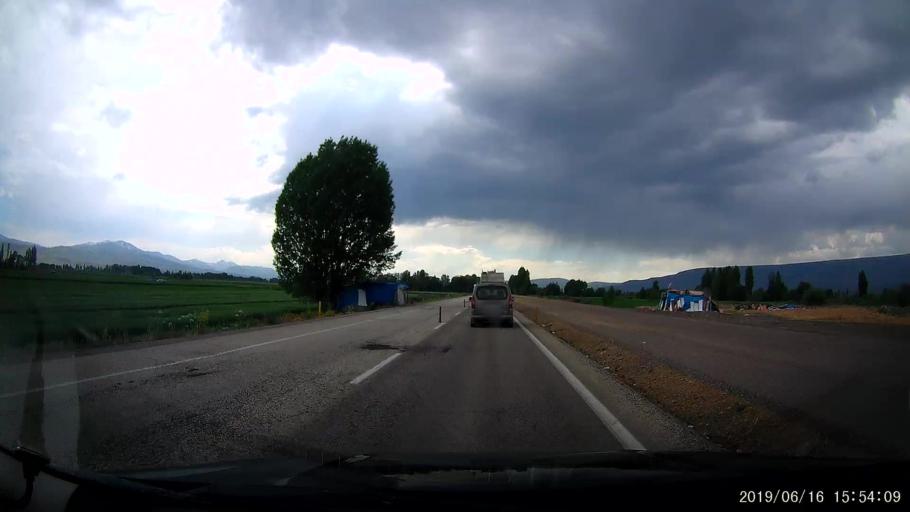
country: TR
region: Erzurum
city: Pasinler
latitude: 39.9775
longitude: 41.6376
